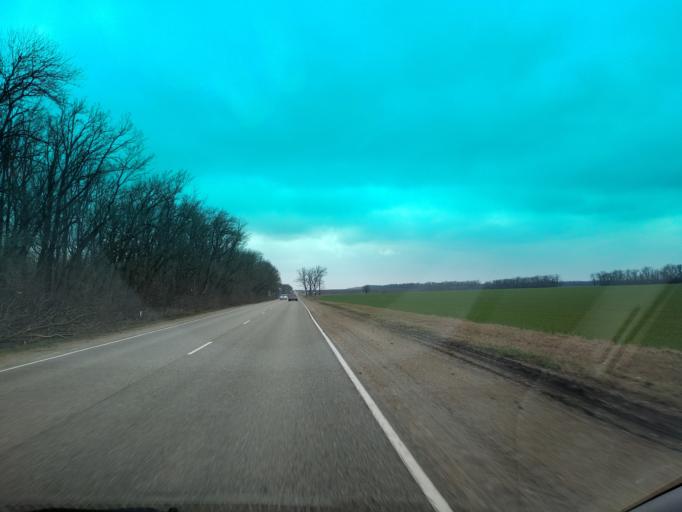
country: RU
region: Krasnodarskiy
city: Novorozhdestvenskaya
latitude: 45.7590
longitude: 39.9266
